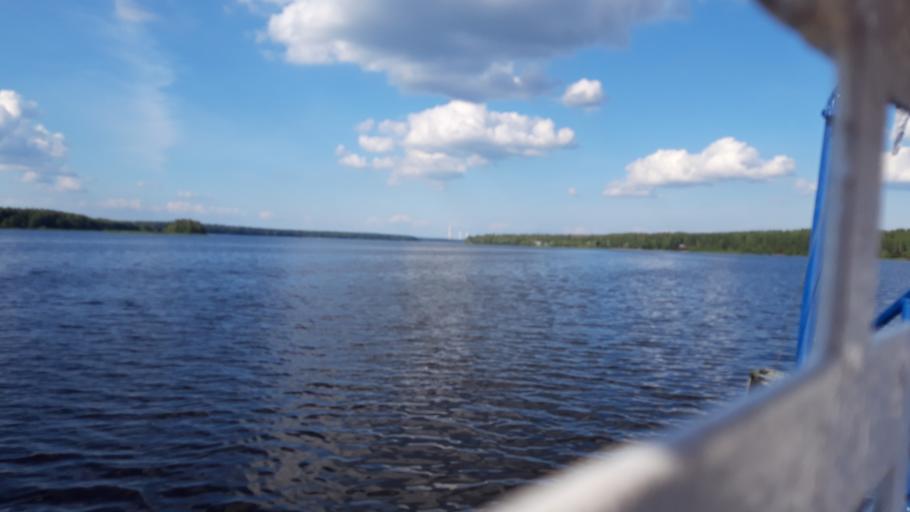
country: RU
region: Tverskaya
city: Konakovo
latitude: 56.6737
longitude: 36.6744
